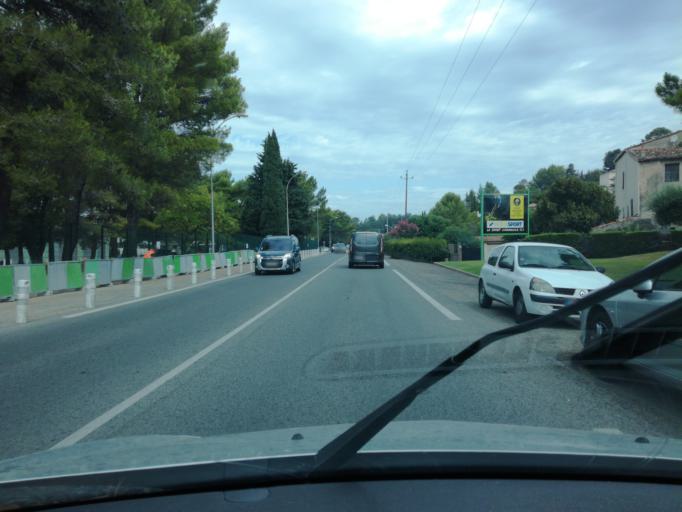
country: FR
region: Provence-Alpes-Cote d'Azur
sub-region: Departement du Var
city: Draguignan
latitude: 43.5239
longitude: 6.4615
